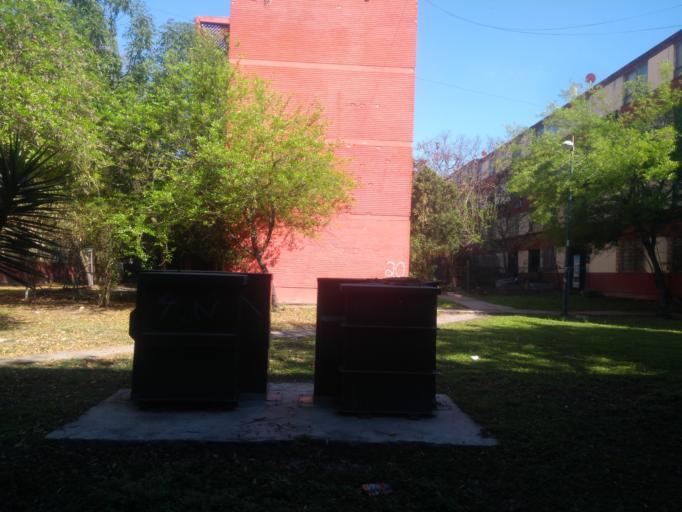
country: MX
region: Nuevo Leon
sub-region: Monterrey
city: Monterrey
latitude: 25.6684
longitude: -100.3025
